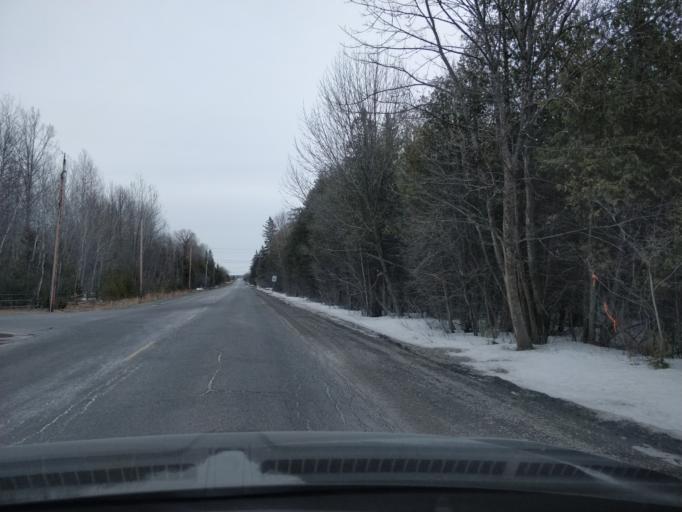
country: CA
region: Ontario
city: Bells Corners
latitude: 45.2393
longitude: -75.8995
